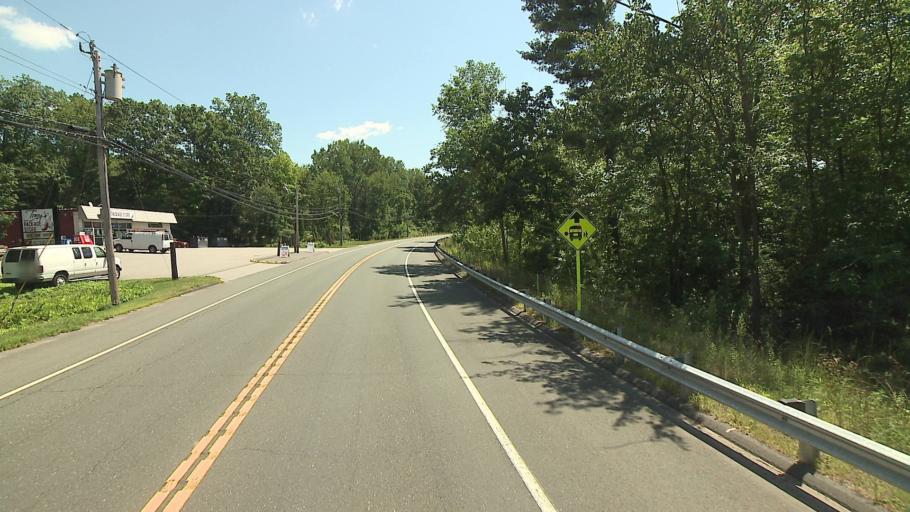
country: US
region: Connecticut
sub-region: Litchfield County
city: Northwest Harwinton
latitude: 41.7974
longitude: -73.0813
